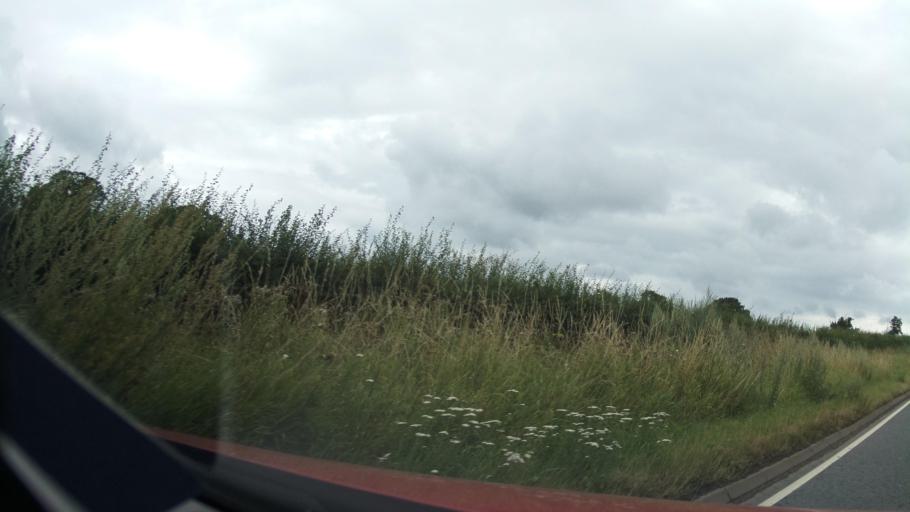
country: GB
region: England
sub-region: Worcestershire
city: Fernhill Heath
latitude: 52.2337
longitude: -2.1719
